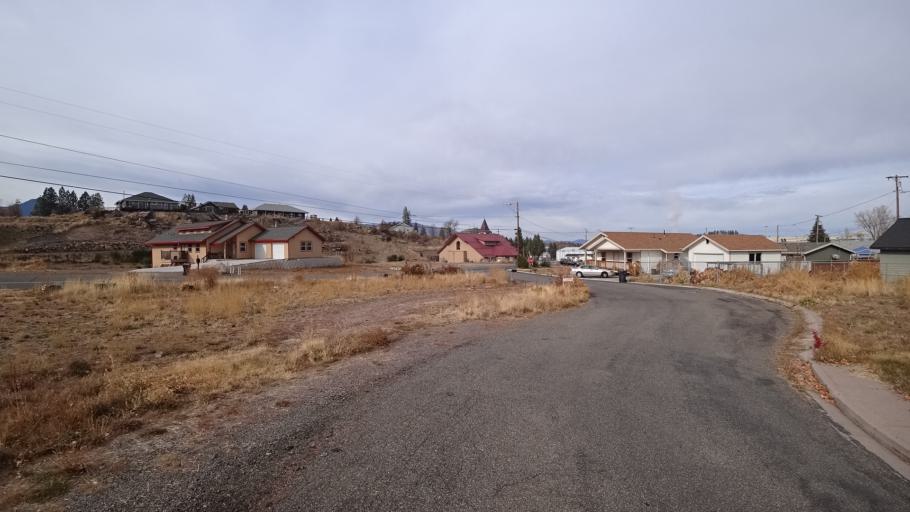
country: US
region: California
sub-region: Siskiyou County
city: Weed
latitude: 41.4301
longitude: -122.3775
